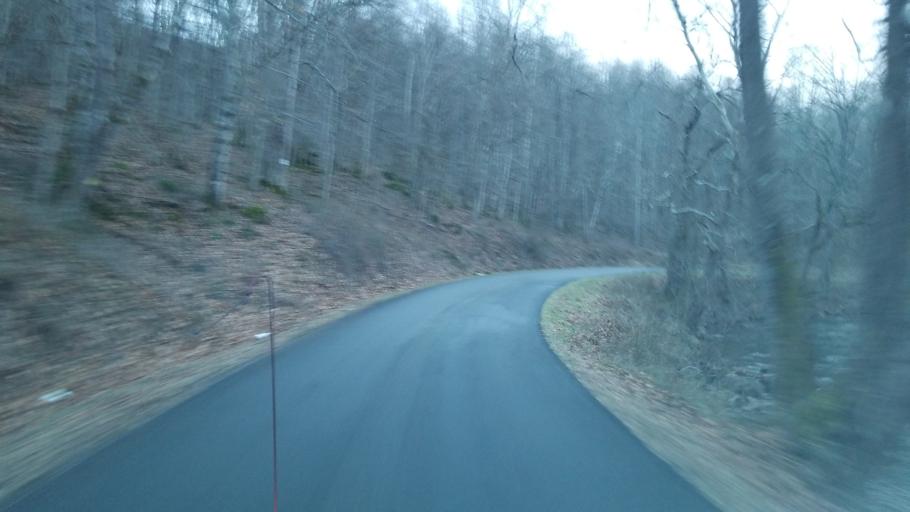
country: US
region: Virginia
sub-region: Pulaski County
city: Pulaski
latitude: 37.1530
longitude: -80.8691
